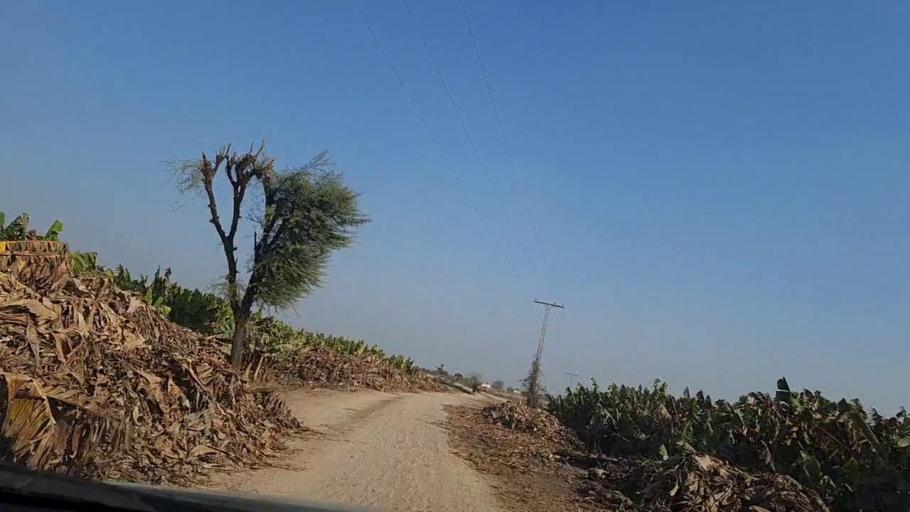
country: PK
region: Sindh
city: Sakrand
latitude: 26.0211
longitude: 68.3261
